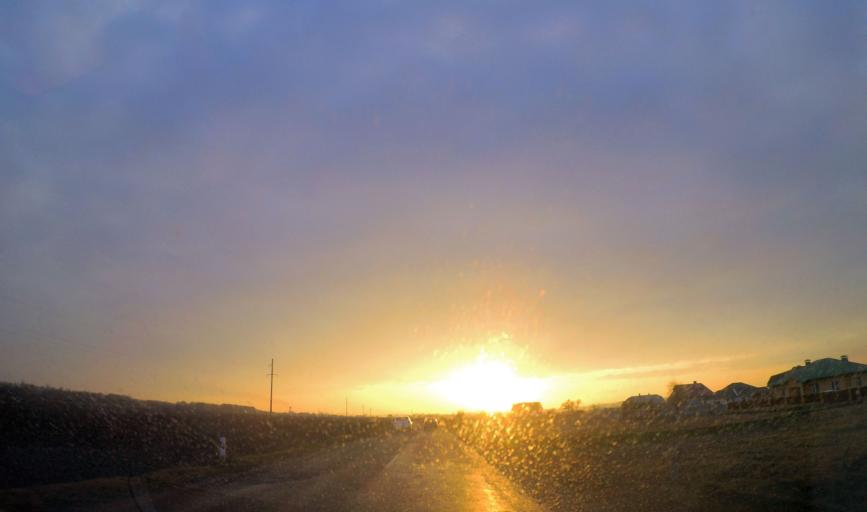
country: BY
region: Grodnenskaya
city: Hrodna
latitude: 53.7516
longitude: 23.9387
